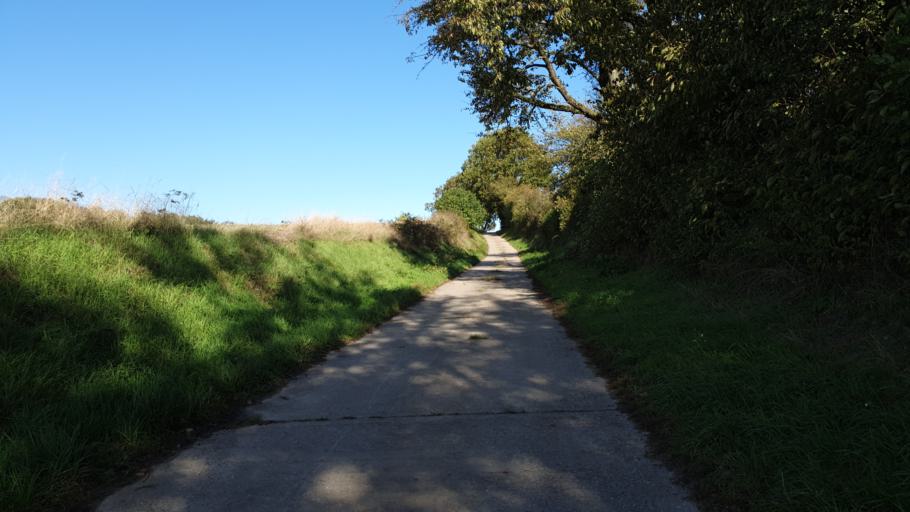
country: DE
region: Rheinland-Pfalz
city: Hergersweiler
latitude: 49.1060
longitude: 8.0903
